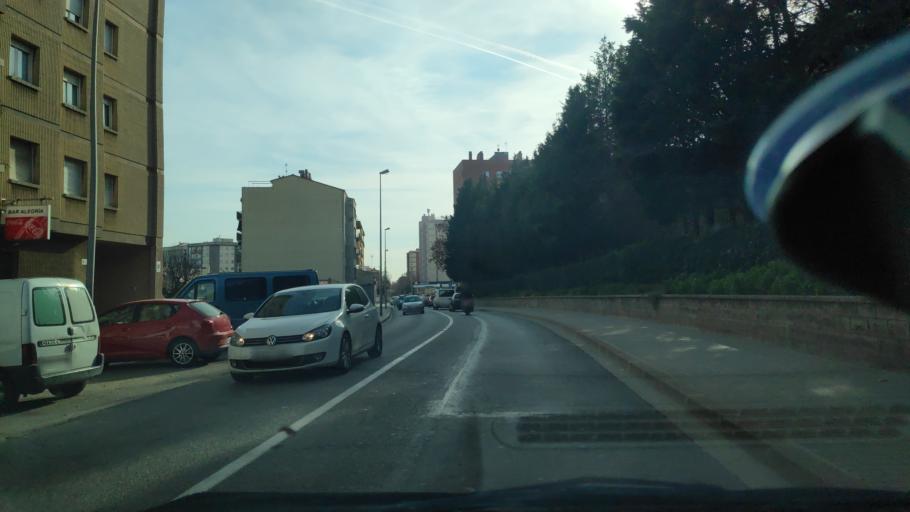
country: ES
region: Catalonia
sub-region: Provincia de Barcelona
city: Sabadell
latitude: 41.5632
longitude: 2.1010
